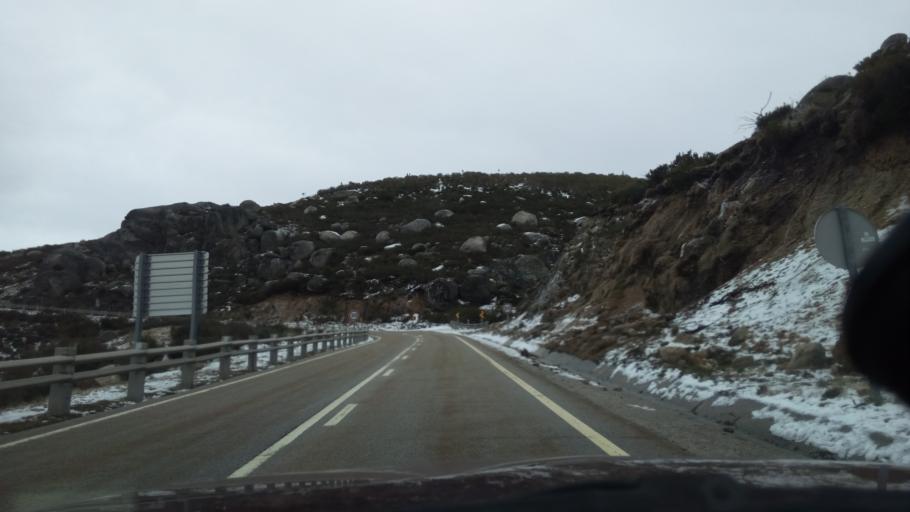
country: PT
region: Guarda
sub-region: Seia
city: Seia
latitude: 40.3587
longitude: -7.6679
